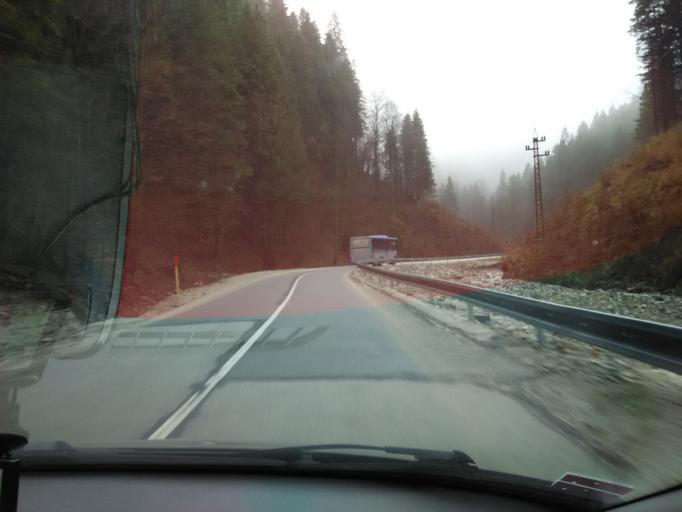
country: SK
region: Zilinsky
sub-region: Okres Zilina
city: Terchova
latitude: 49.2149
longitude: 19.0377
